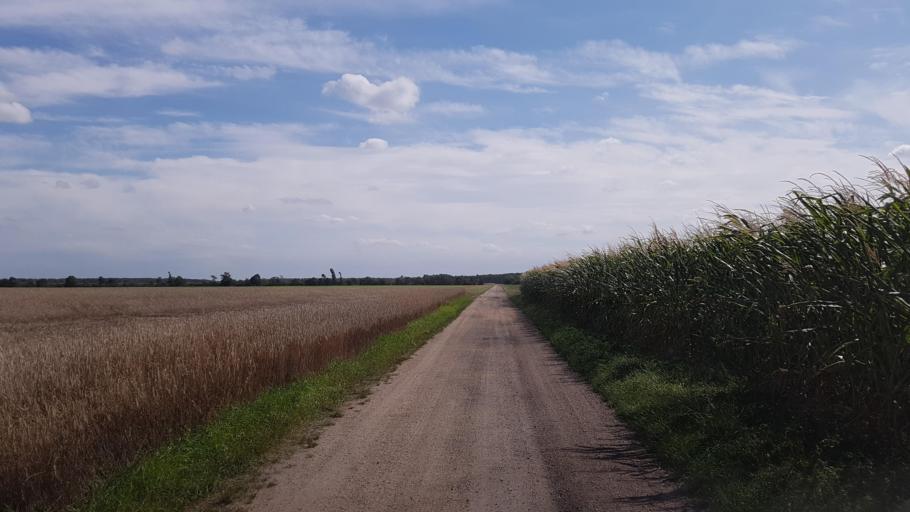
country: DE
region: Brandenburg
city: Muhlberg
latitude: 51.4613
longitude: 13.2826
